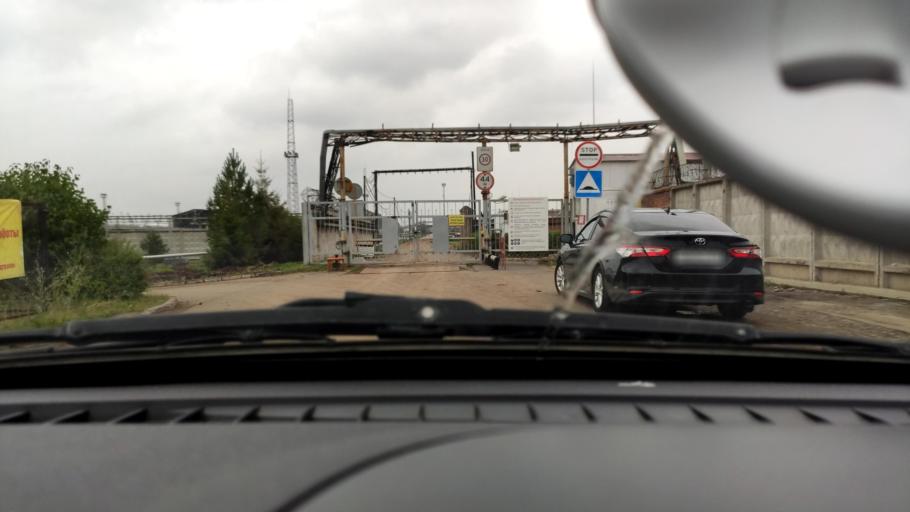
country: RU
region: Perm
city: Gamovo
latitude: 57.9074
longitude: 56.1503
